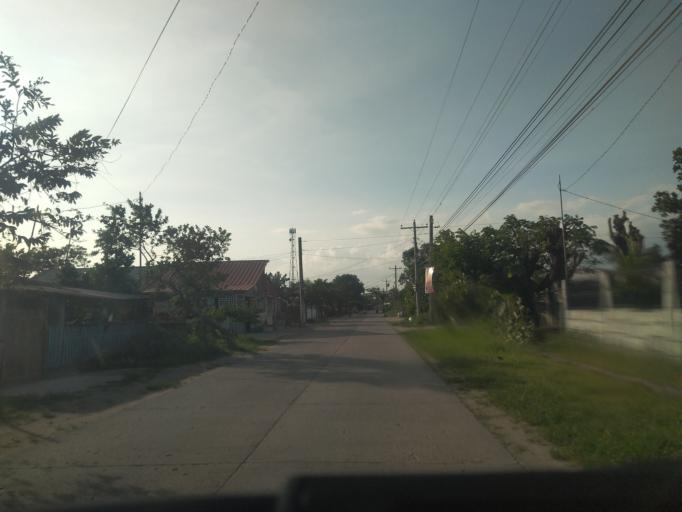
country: PH
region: Central Luzon
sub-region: Province of Pampanga
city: Bulaon
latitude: 15.0883
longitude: 120.6916
